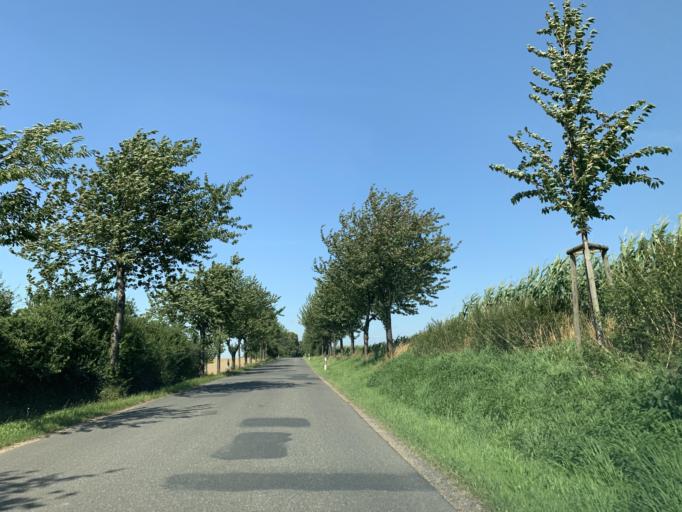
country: DE
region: Mecklenburg-Vorpommern
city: Loitz
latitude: 53.3443
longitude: 13.3910
